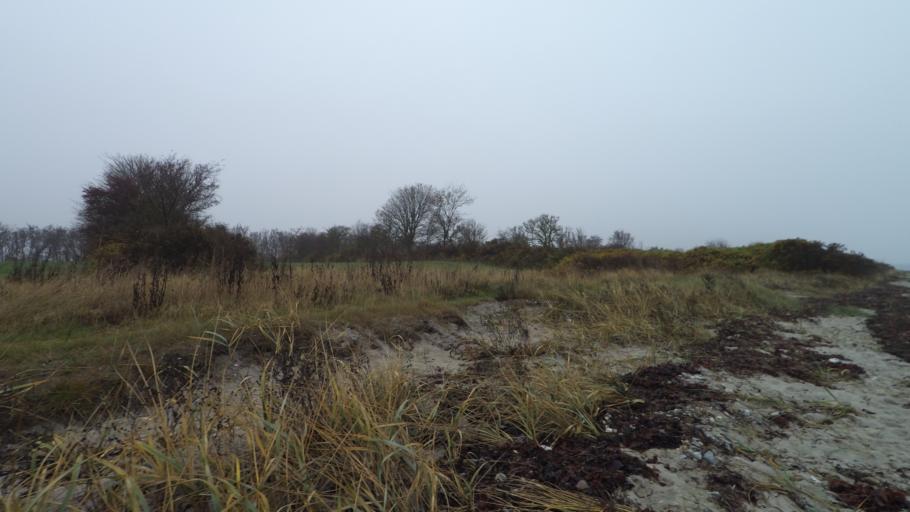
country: DK
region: Central Jutland
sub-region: Odder Kommune
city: Odder
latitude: 55.9359
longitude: 10.2601
